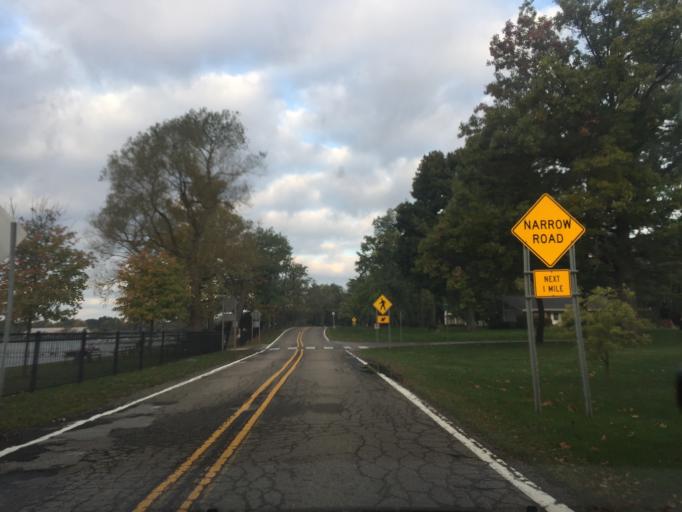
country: US
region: Michigan
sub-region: Oakland County
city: Sylvan Lake
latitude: 42.5948
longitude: -83.3326
